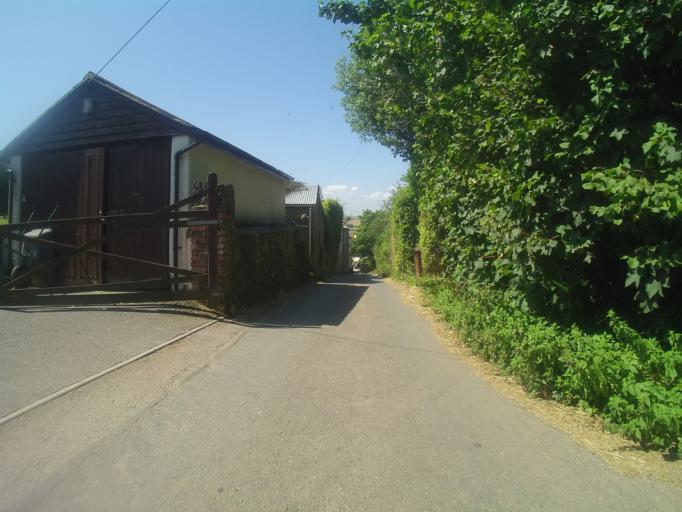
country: GB
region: England
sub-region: Devon
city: Dartmouth
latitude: 50.3663
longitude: -3.6356
